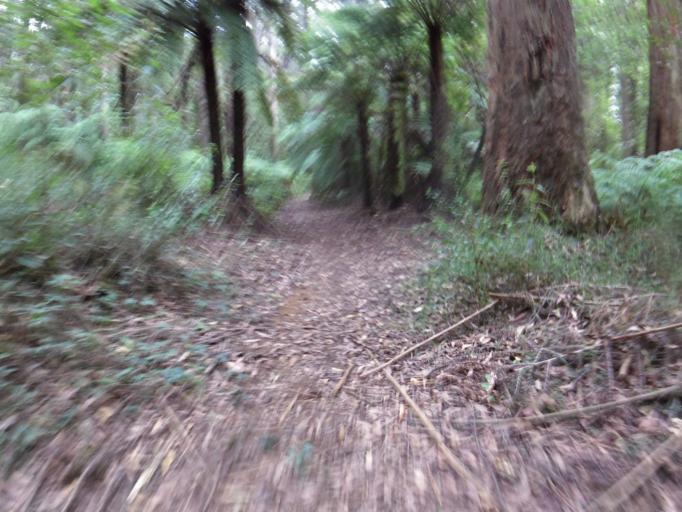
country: AU
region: Victoria
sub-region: Yarra Ranges
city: Healesville
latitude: -37.5410
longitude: 145.4823
